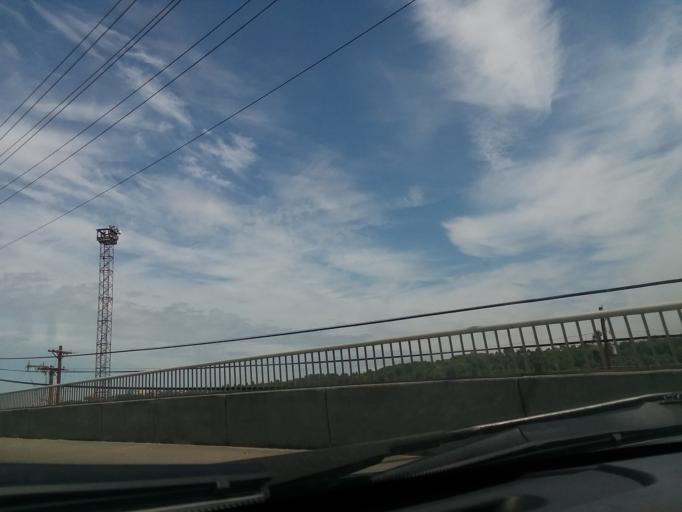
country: US
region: Washington
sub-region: King County
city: Seattle
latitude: 47.5616
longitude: -122.3340
